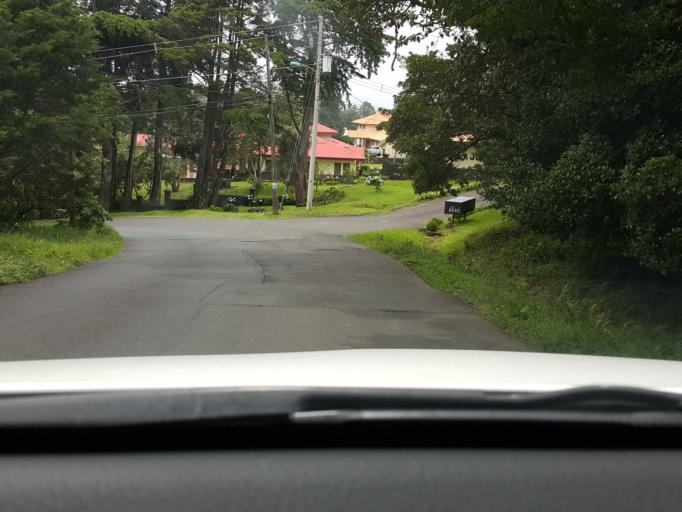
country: CR
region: Heredia
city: San Josecito
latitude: 10.0583
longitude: -84.0907
